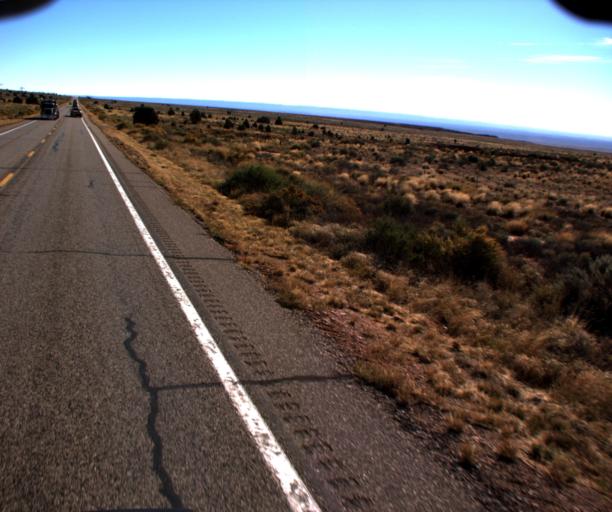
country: US
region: Arizona
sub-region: Coconino County
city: Fredonia
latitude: 36.8579
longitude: -112.7607
